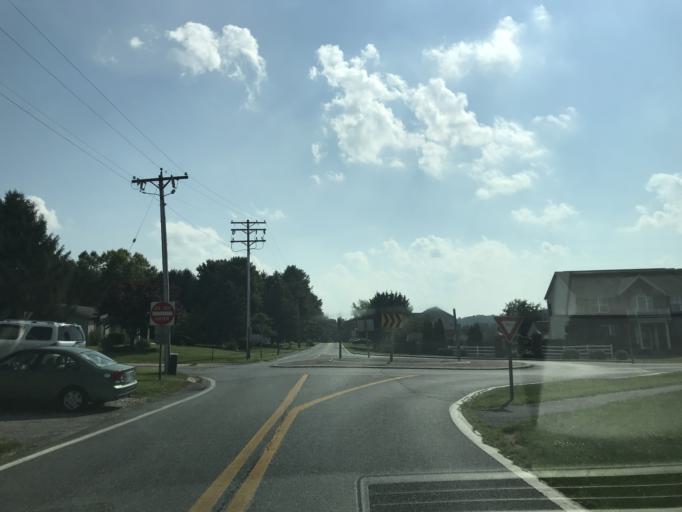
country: US
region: Maryland
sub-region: Carroll County
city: Manchester
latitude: 39.6738
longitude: -76.8939
